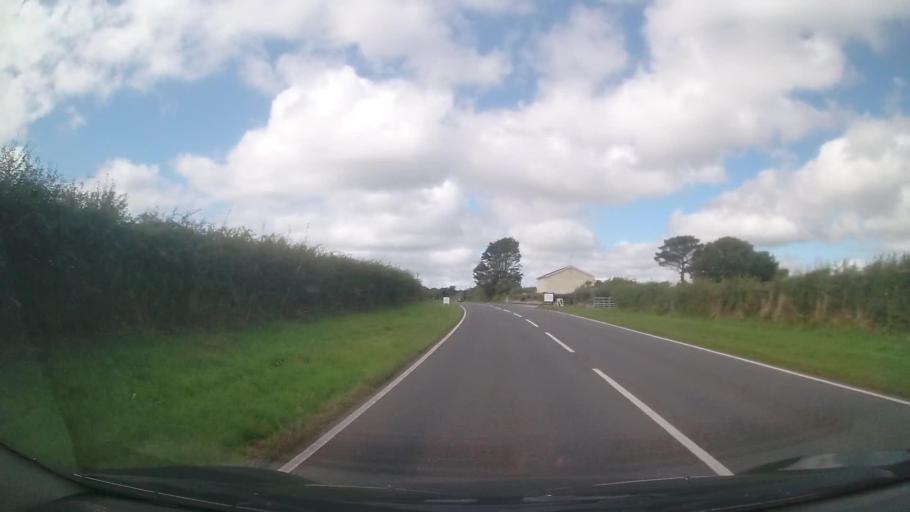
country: GB
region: Wales
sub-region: Pembrokeshire
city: Manorbier
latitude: 51.6519
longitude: -4.7730
